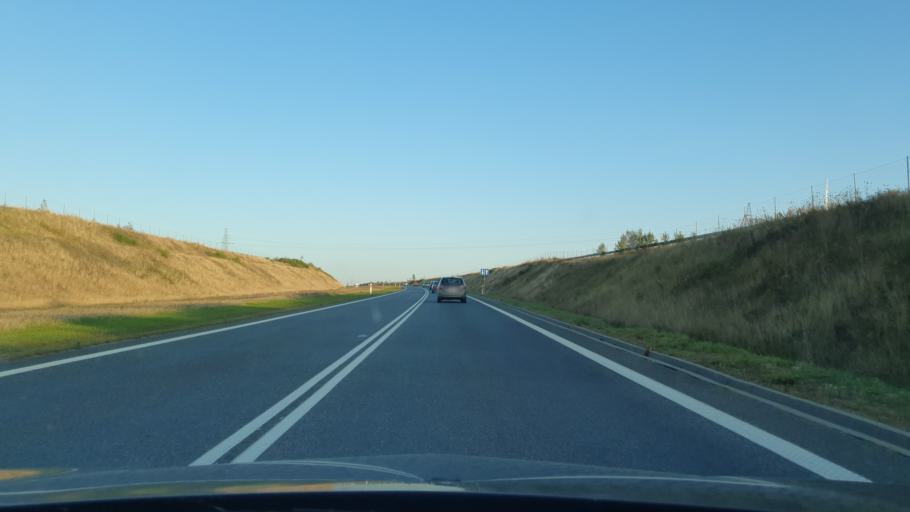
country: PL
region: Pomeranian Voivodeship
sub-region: Powiat slupski
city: Kobylnica
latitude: 54.4283
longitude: 16.9807
